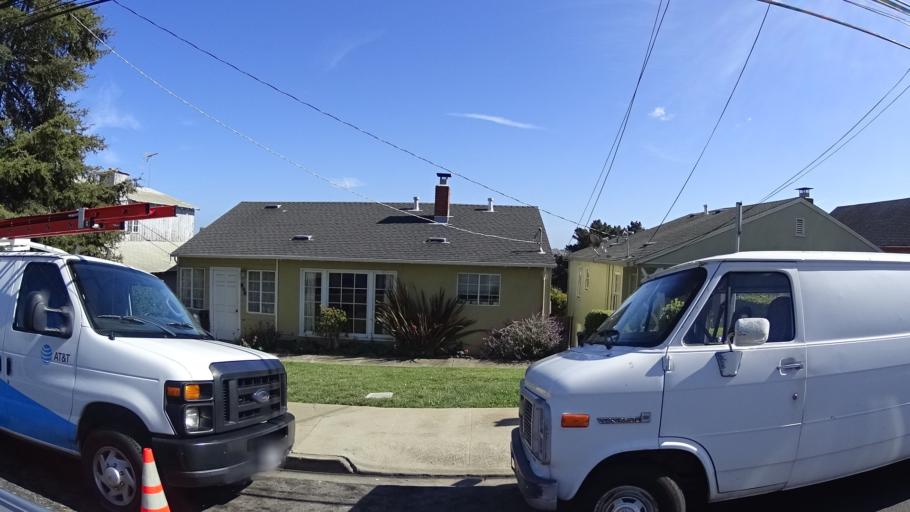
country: US
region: California
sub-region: San Mateo County
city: South San Francisco
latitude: 37.6612
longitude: -122.4105
